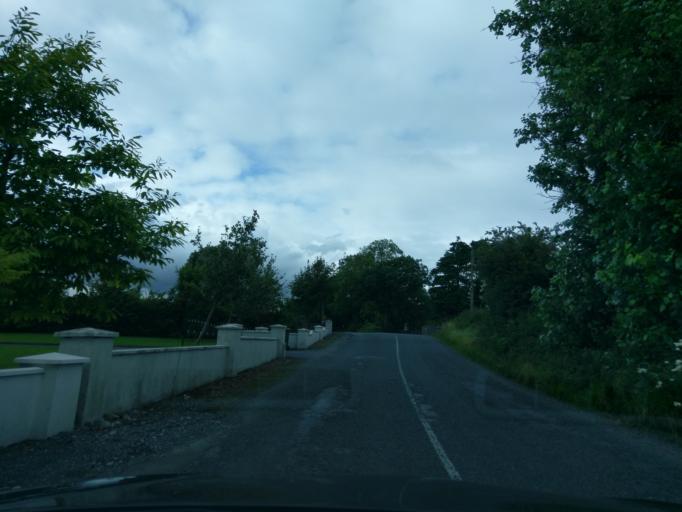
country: IE
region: Connaught
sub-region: County Galway
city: Athenry
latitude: 53.2434
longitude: -8.7482
